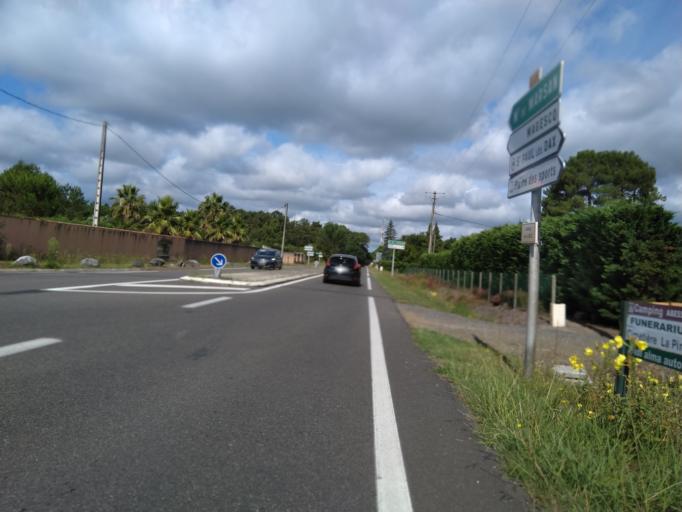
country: FR
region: Aquitaine
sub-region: Departement des Landes
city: Mees
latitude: 43.7319
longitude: -1.0997
